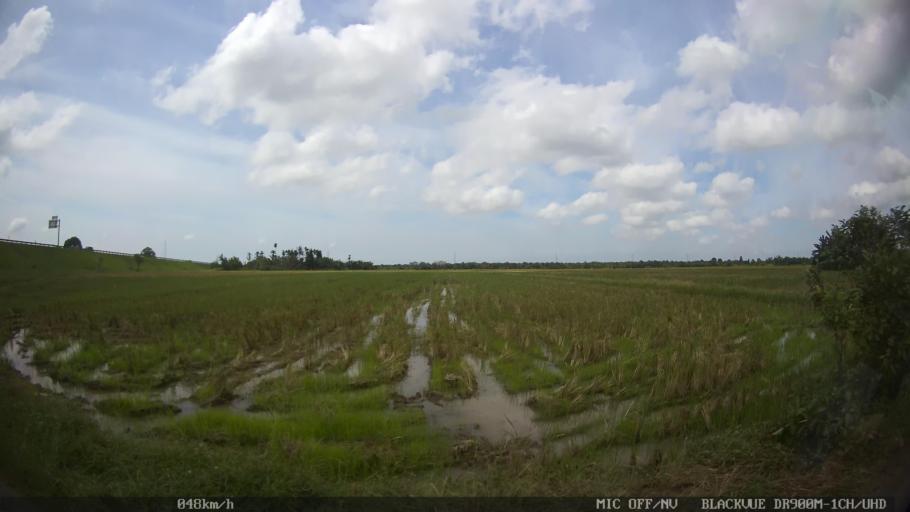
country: ID
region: North Sumatra
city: Percut
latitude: 3.5720
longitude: 98.8480
